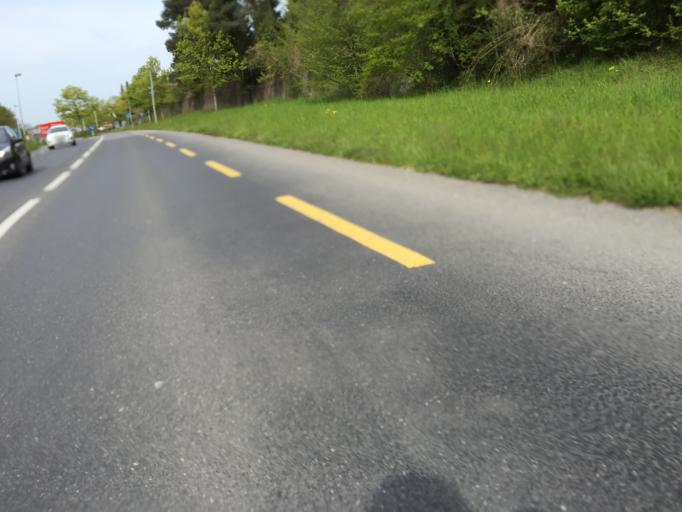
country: CH
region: Fribourg
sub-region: Sense District
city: Flamatt
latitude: 46.8941
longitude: 7.3256
